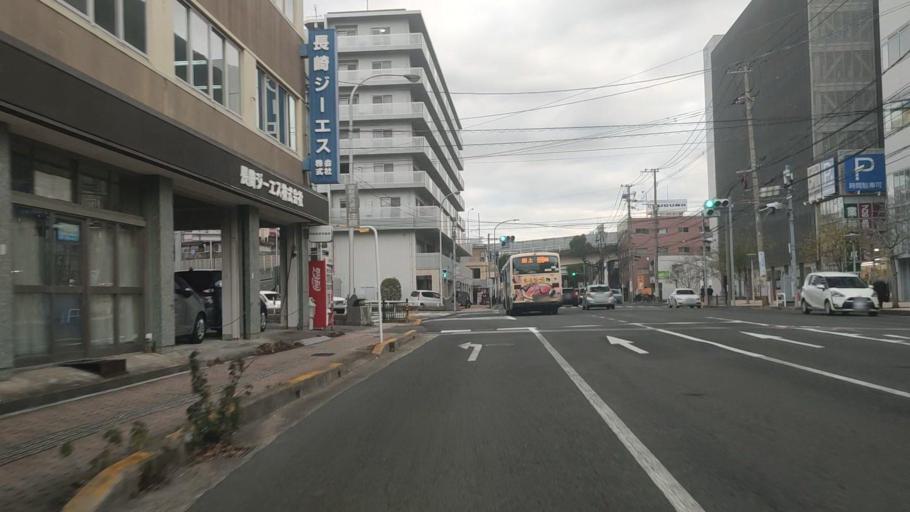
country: JP
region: Nagasaki
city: Nagasaki-shi
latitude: 32.7500
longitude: 129.8646
